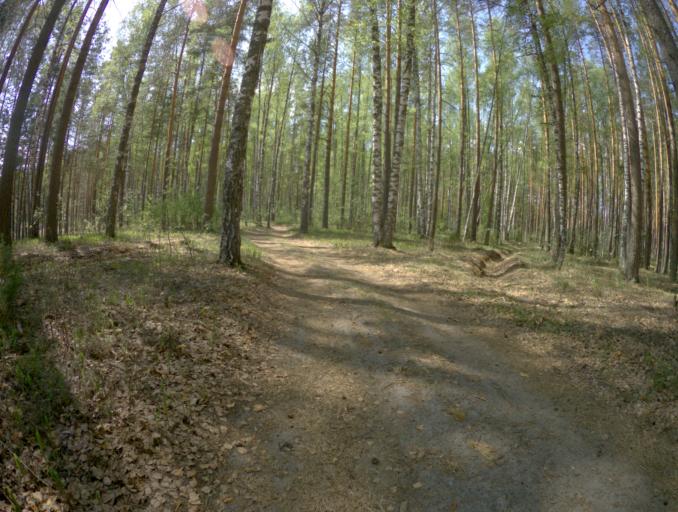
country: RU
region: Ivanovo
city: Talitsy
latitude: 56.4745
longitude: 42.1853
